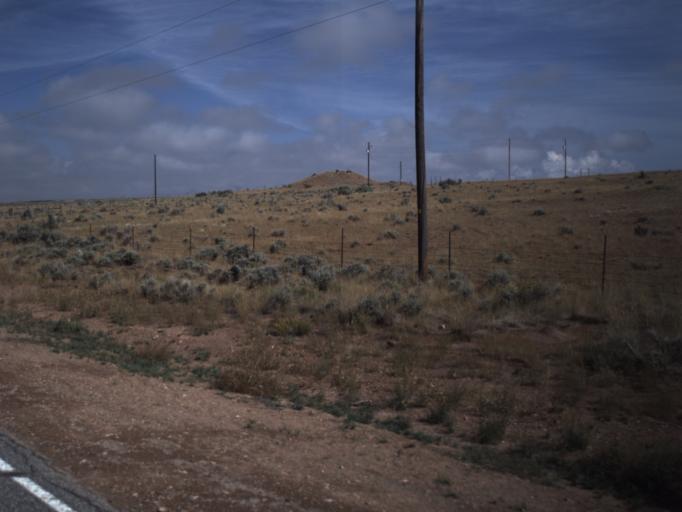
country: US
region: Wyoming
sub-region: Uinta County
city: Evanston
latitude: 41.4226
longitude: -111.0518
